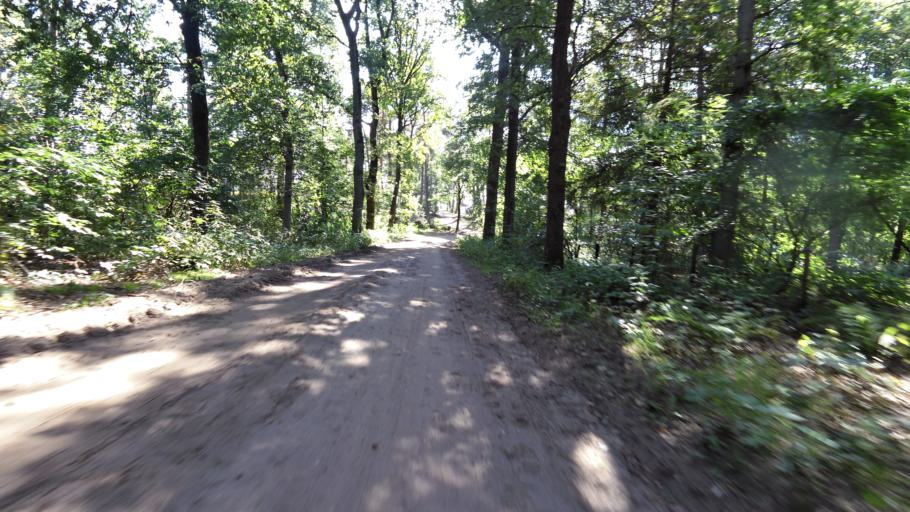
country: NL
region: Gelderland
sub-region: Gemeente Renkum
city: Renkum
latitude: 51.9983
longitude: 5.7394
